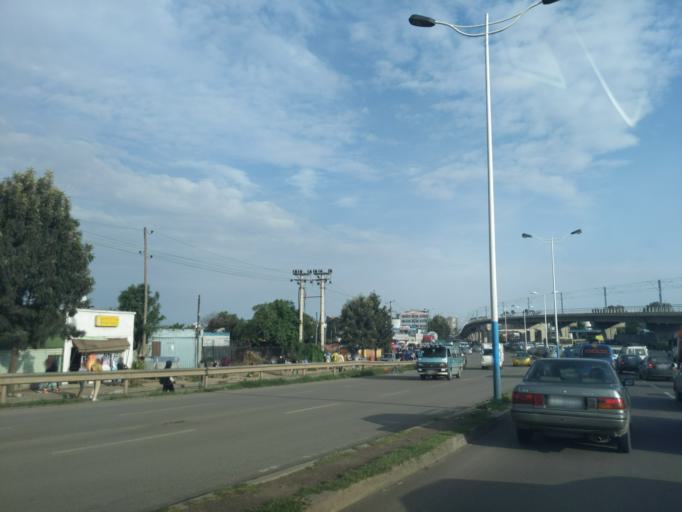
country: ET
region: Adis Abeba
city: Addis Ababa
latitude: 8.9783
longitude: 38.7595
